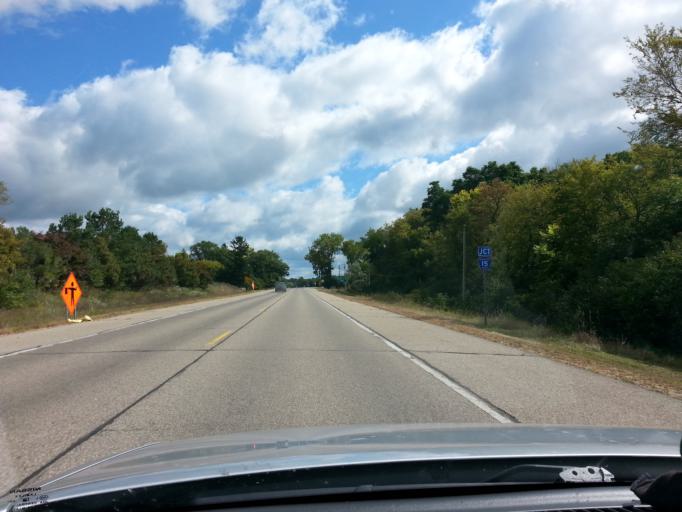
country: US
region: Minnesota
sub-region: Washington County
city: Lake Elmo
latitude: 44.9635
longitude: -92.8663
